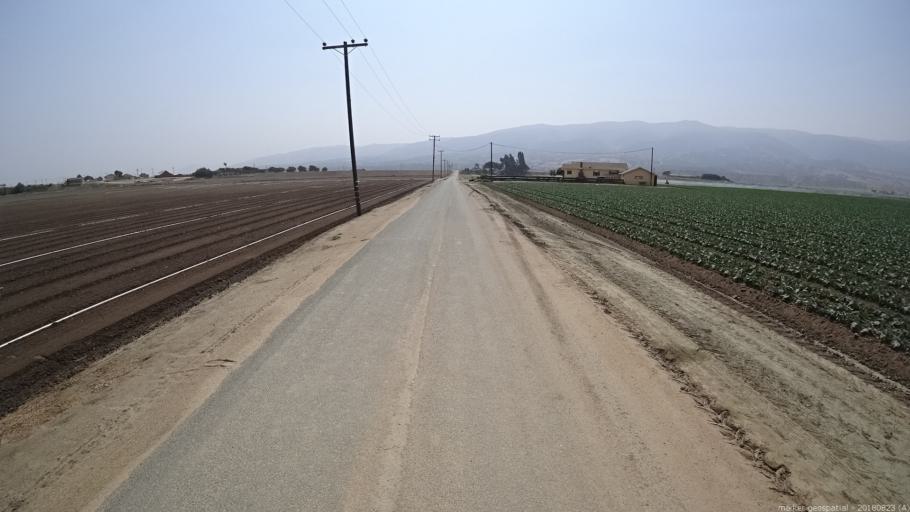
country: US
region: California
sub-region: Monterey County
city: Soledad
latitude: 36.4089
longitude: -121.3477
